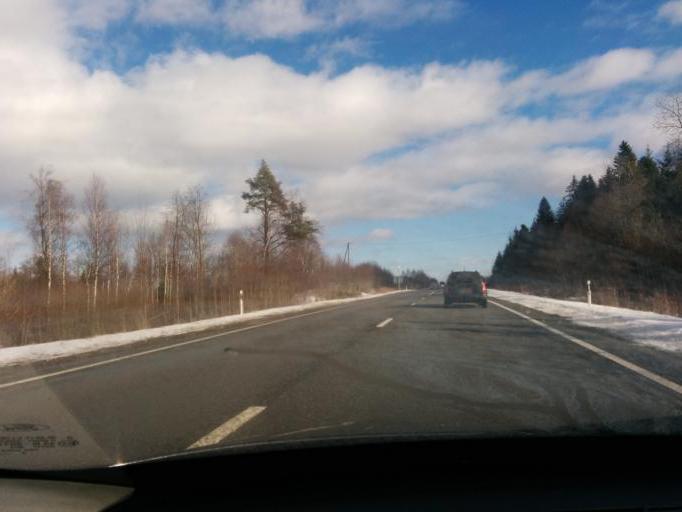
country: LV
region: Raunas
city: Rauna
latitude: 57.3068
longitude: 25.6220
